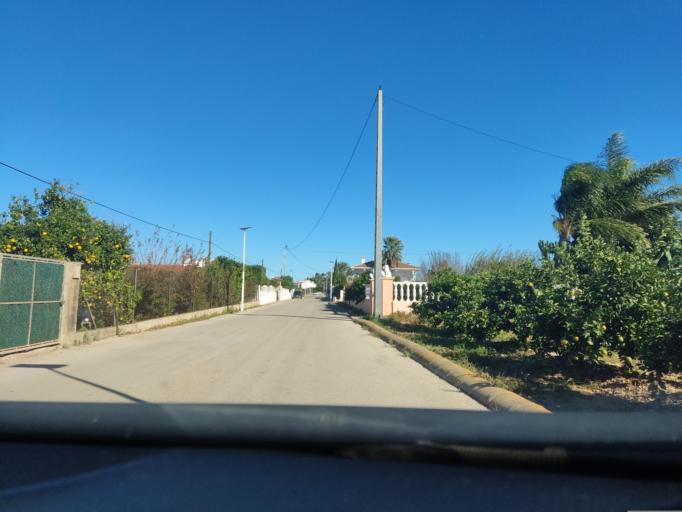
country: ES
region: Valencia
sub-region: Provincia de Alicante
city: els Poblets
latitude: 38.8546
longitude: 0.0271
